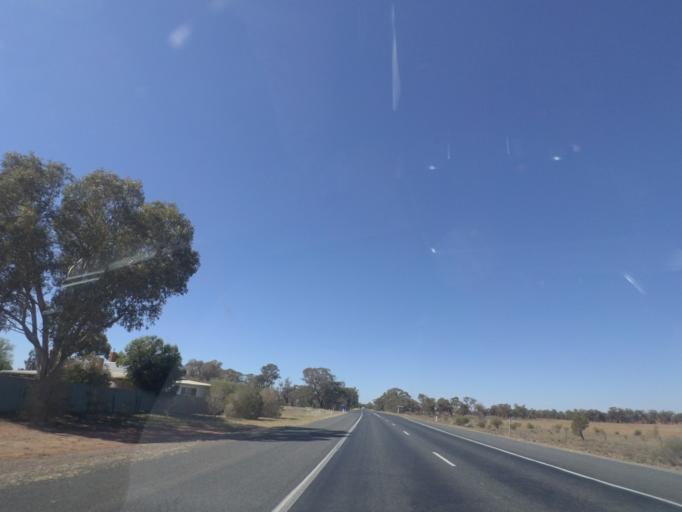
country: AU
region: New South Wales
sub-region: Bland
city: West Wyalong
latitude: -34.1925
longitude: 147.1114
